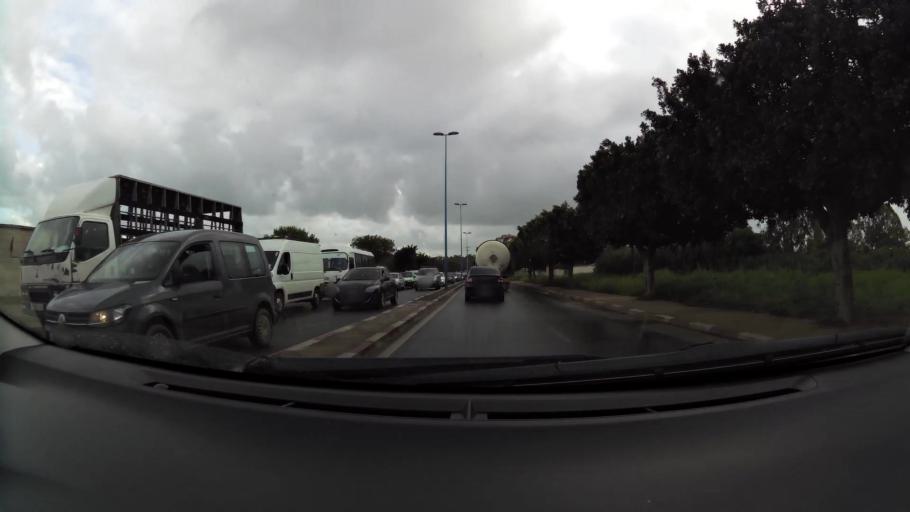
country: MA
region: Grand Casablanca
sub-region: Mohammedia
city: Mohammedia
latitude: 33.6809
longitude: -7.4083
